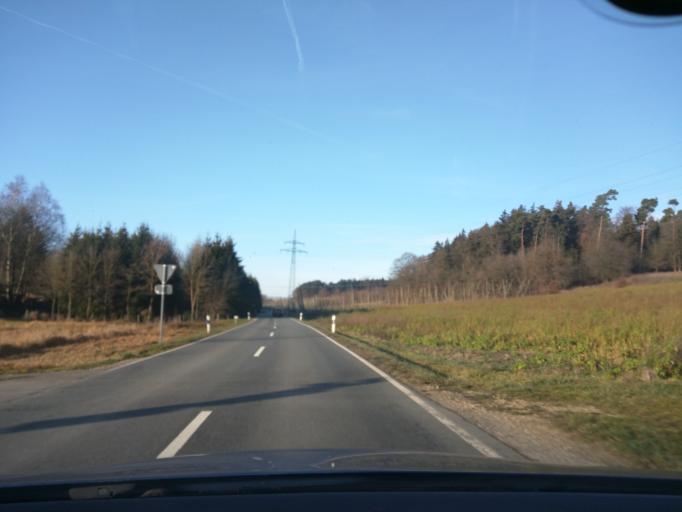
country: DE
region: Bavaria
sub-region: Upper Bavaria
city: Au in der Hallertau
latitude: 48.5672
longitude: 11.7387
